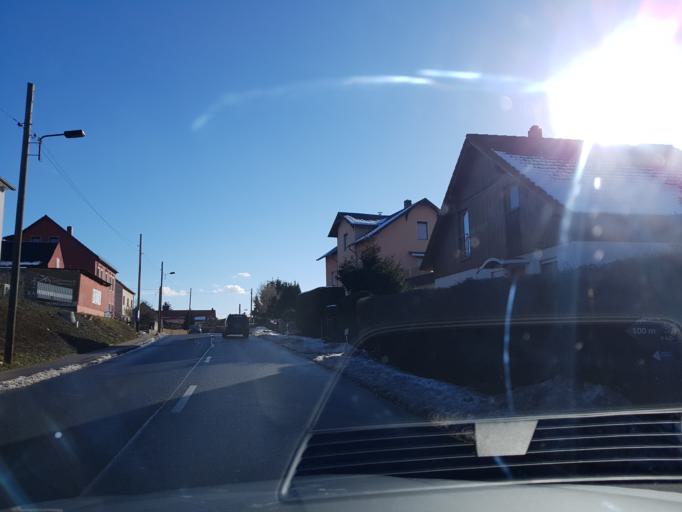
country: DE
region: Saxony
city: Radebeul
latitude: 51.1190
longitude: 13.6940
